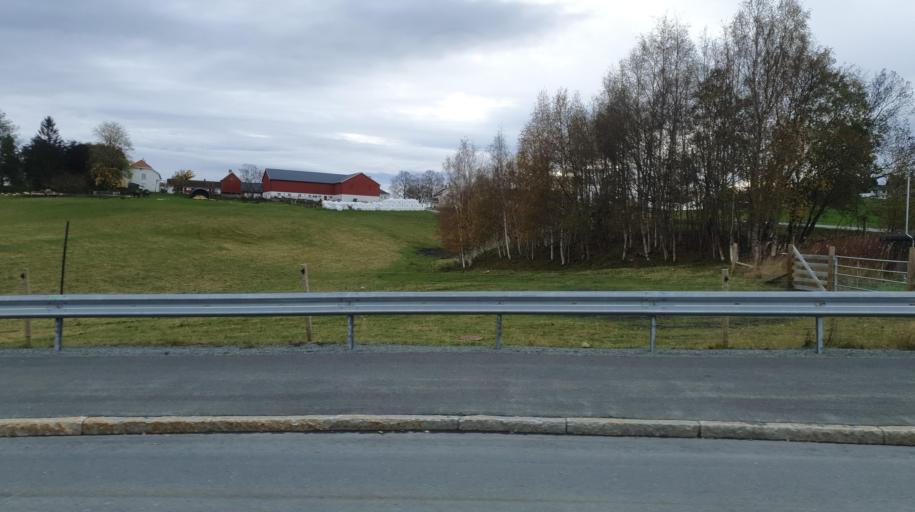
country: NO
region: Sor-Trondelag
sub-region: Klaebu
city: Klaebu
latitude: 63.2985
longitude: 10.4761
